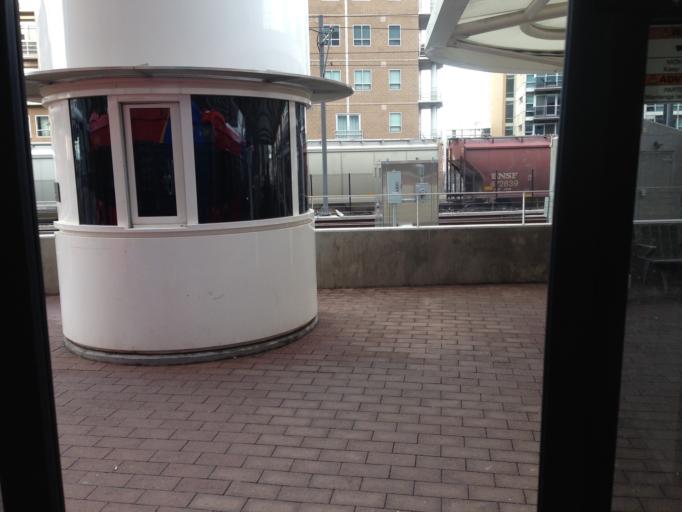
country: US
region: Colorado
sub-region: Denver County
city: Denver
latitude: 39.7548
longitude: -105.0034
